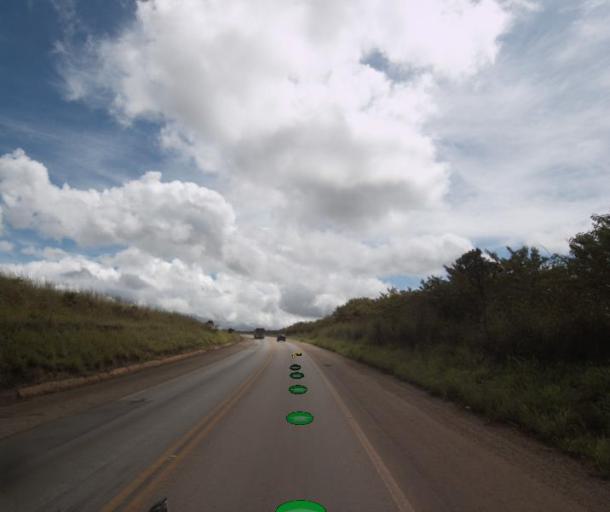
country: BR
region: Federal District
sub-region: Brasilia
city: Brasilia
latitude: -15.7455
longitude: -48.3547
